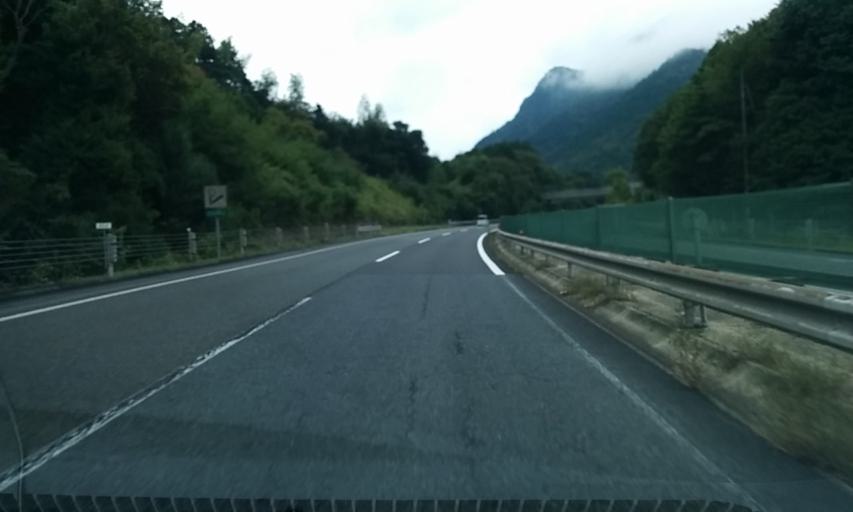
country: JP
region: Hyogo
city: Sasayama
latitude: 35.1405
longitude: 135.1346
